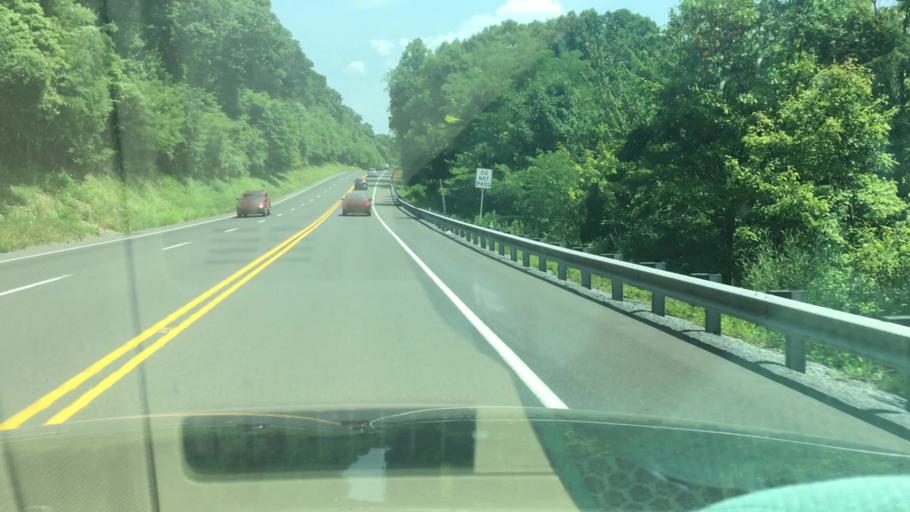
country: US
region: Pennsylvania
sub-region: Carbon County
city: Summit Hill
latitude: 40.7114
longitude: -75.7950
